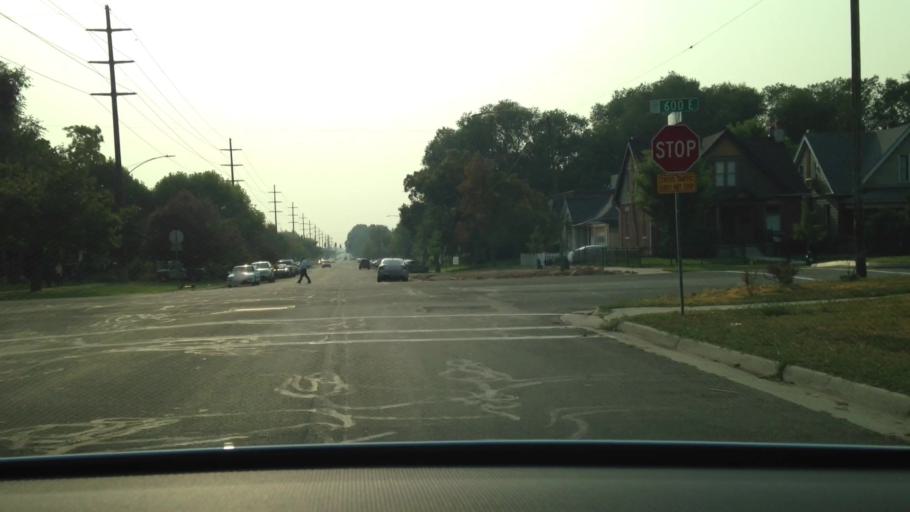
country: US
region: Utah
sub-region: Salt Lake County
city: Salt Lake City
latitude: 40.7542
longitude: -111.8735
